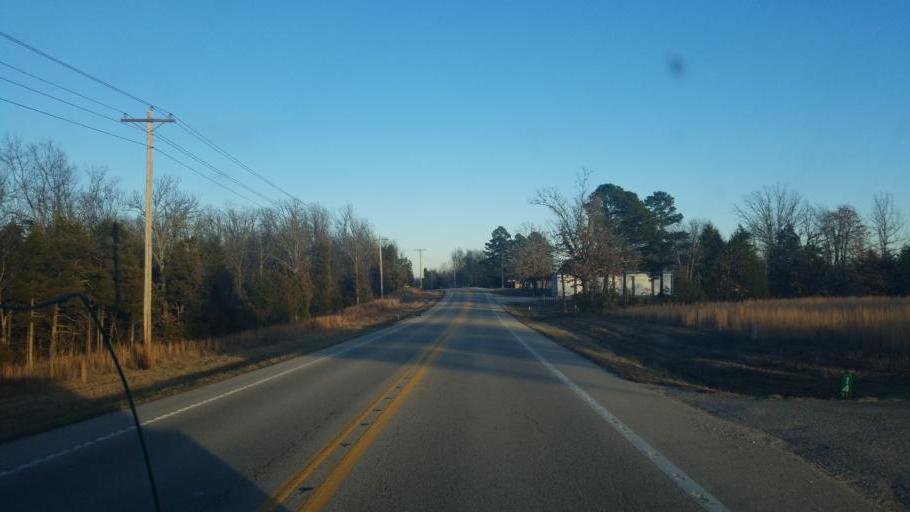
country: US
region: Arkansas
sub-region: Baxter County
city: Mountain Home
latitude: 36.3838
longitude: -92.1708
